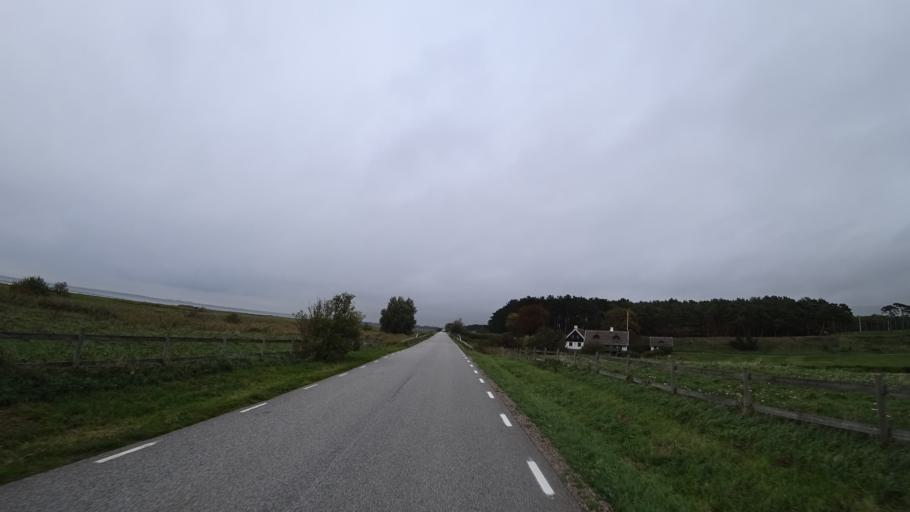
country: SE
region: Skane
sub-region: Kavlinge Kommun
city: Hofterup
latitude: 55.7890
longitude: 12.9383
